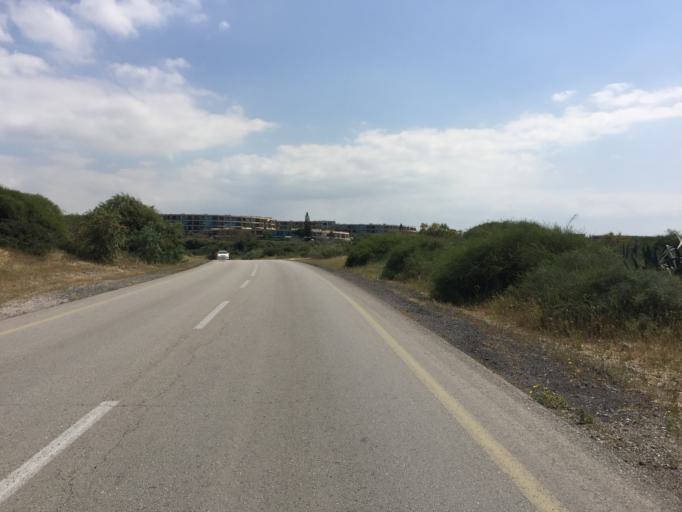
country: IL
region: Haifa
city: Qesarya
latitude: 32.4918
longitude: 34.8995
